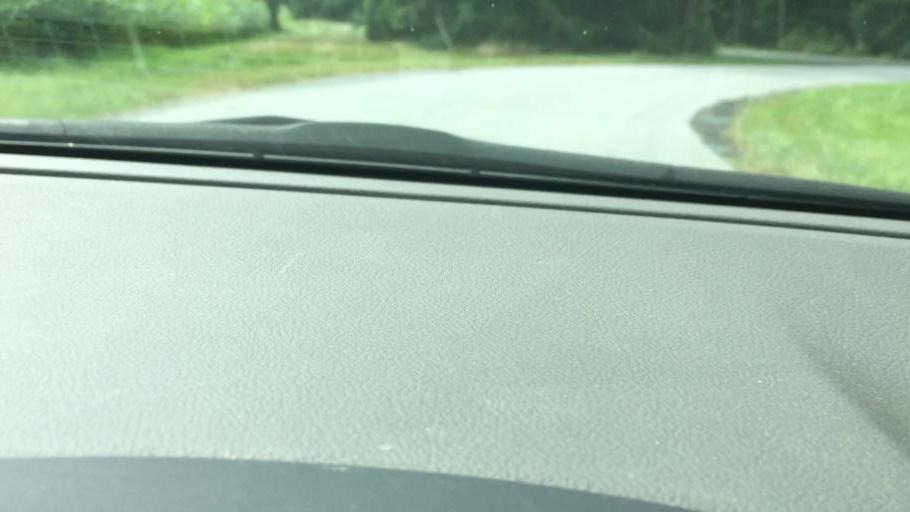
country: US
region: Maryland
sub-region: Worcester County
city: Pocomoke City
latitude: 38.0661
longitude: -75.5076
